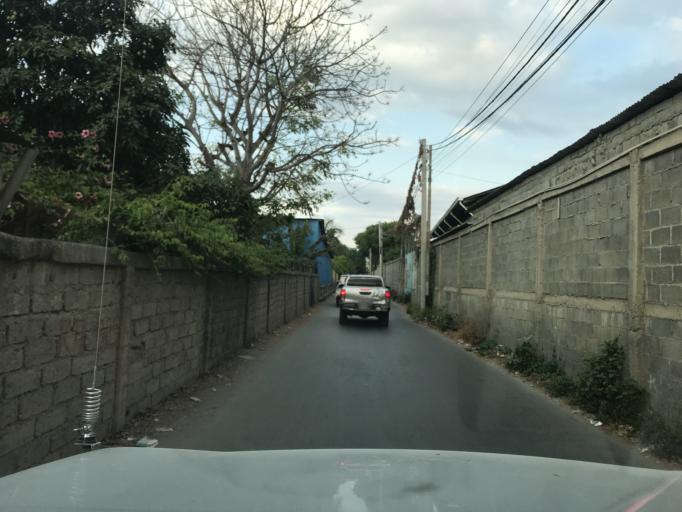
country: TL
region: Dili
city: Dili
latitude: -8.5516
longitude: 125.5412
